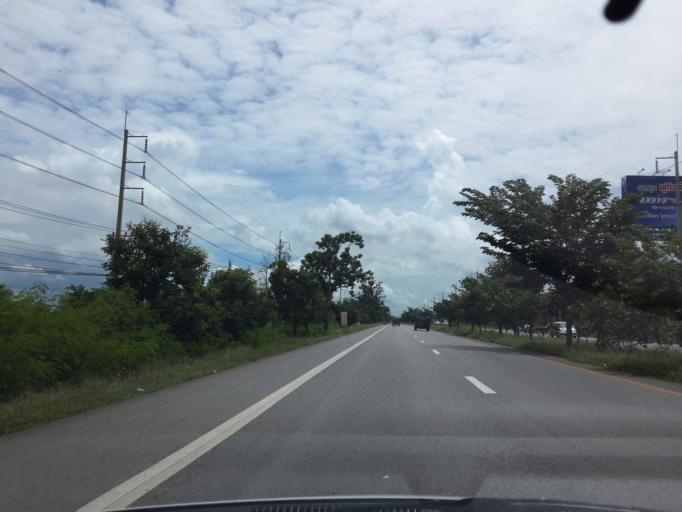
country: TH
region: Ratchaburi
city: Pak Tho
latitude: 13.3797
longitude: 99.8202
